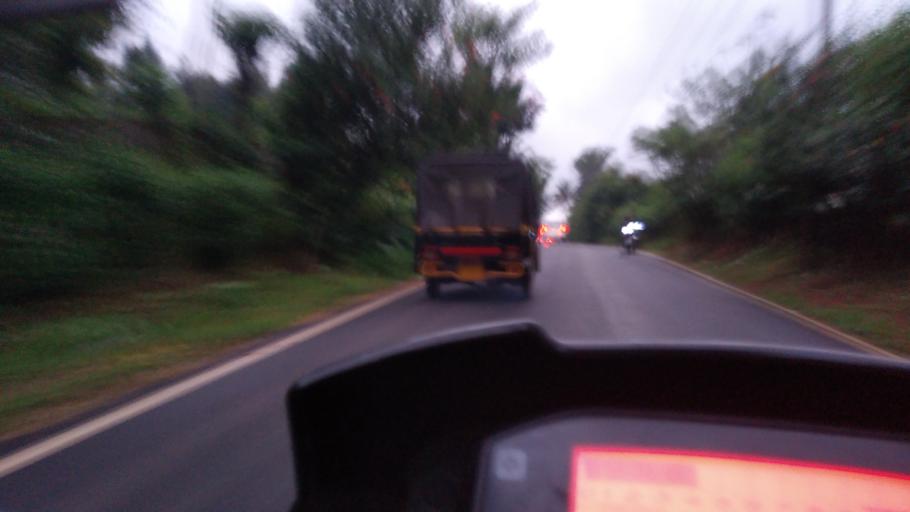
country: IN
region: Kerala
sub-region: Idukki
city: Munnar
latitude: 9.9584
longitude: 77.0913
